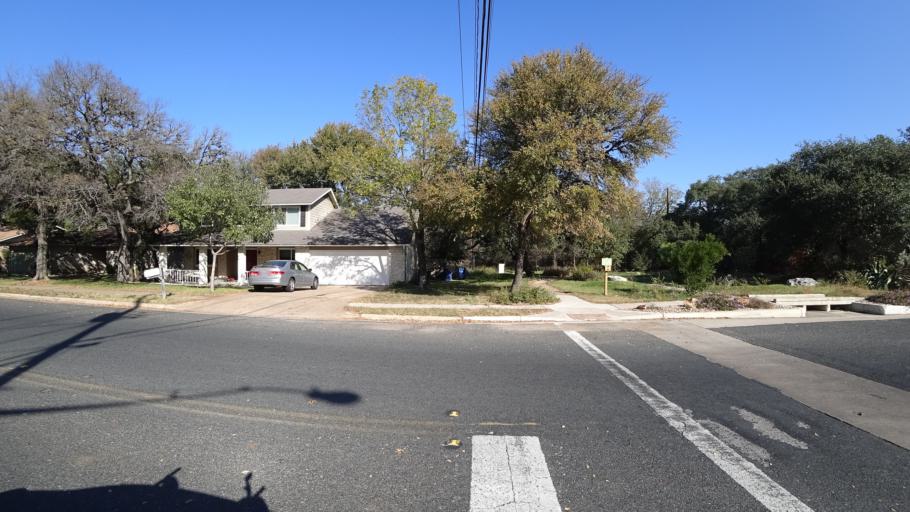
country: US
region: Texas
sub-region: Travis County
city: Barton Creek
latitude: 30.2288
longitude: -97.8434
